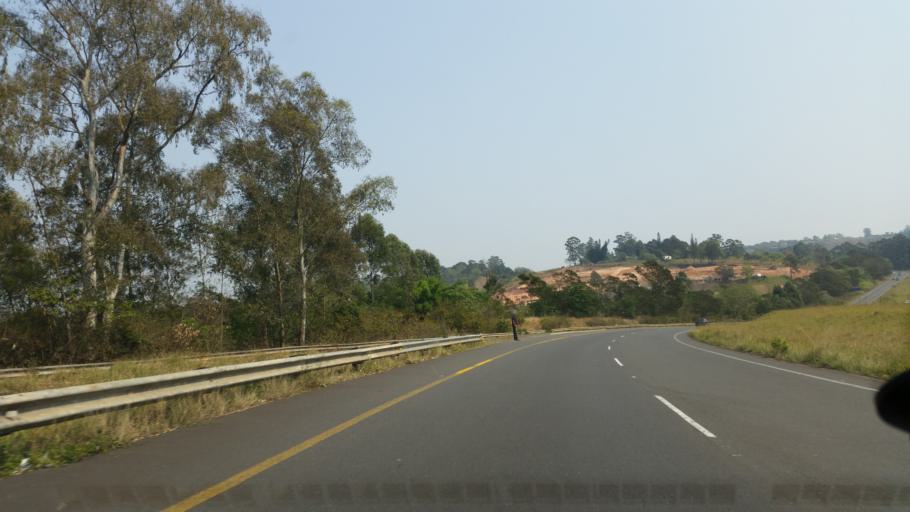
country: ZA
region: KwaZulu-Natal
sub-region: eThekwini Metropolitan Municipality
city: Mpumalanga
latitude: -29.7935
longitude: 30.7399
